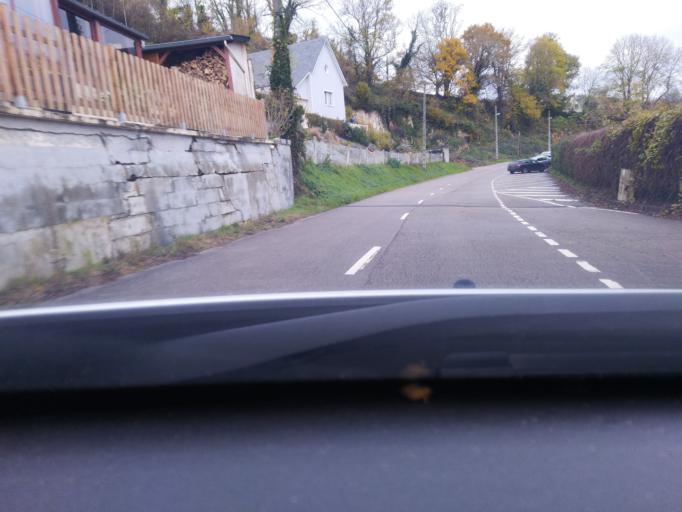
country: FR
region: Haute-Normandie
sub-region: Departement de la Seine-Maritime
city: Duclair
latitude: 49.4834
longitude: 0.8704
